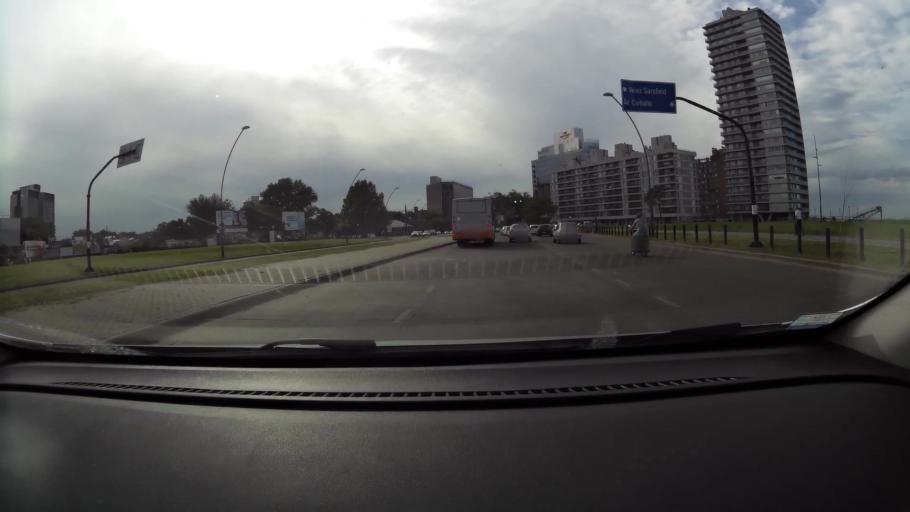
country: AR
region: Santa Fe
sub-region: Departamento de Rosario
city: Rosario
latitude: -32.9246
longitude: -60.6626
